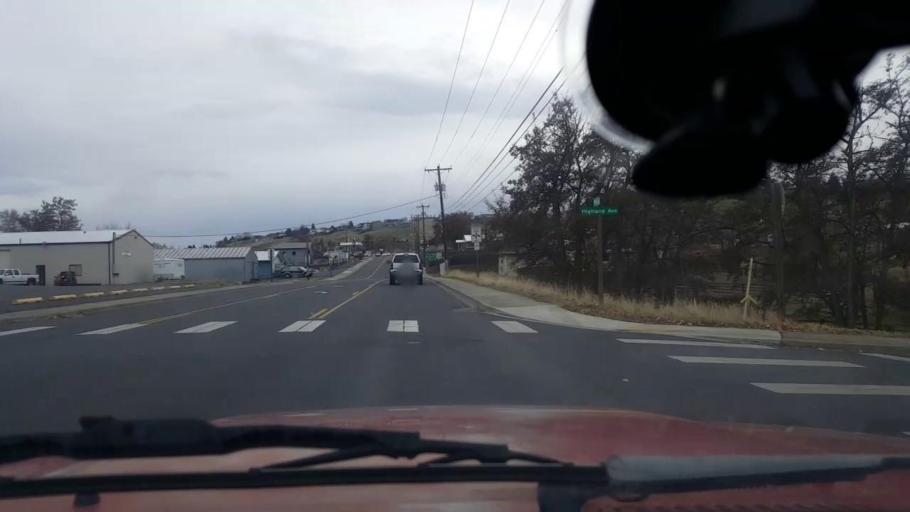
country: US
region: Washington
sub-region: Asotin County
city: West Clarkston-Highland
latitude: 46.4039
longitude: -117.0691
